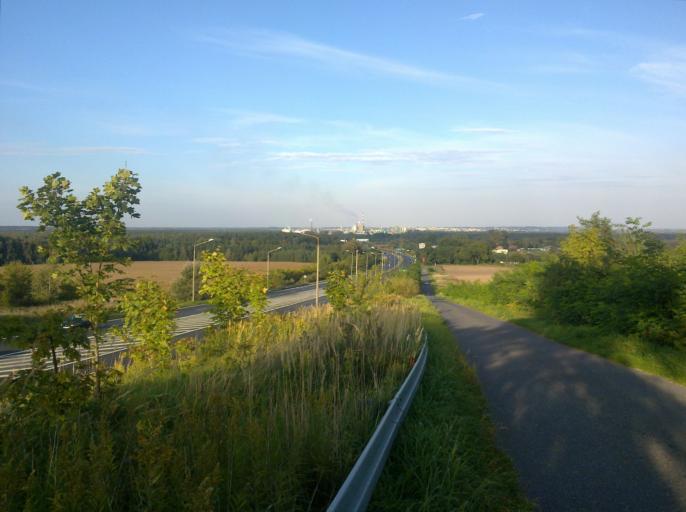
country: PL
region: Kujawsko-Pomorskie
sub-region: Powiat chelminski
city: Chelmno
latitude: 53.3722
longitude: 18.3338
